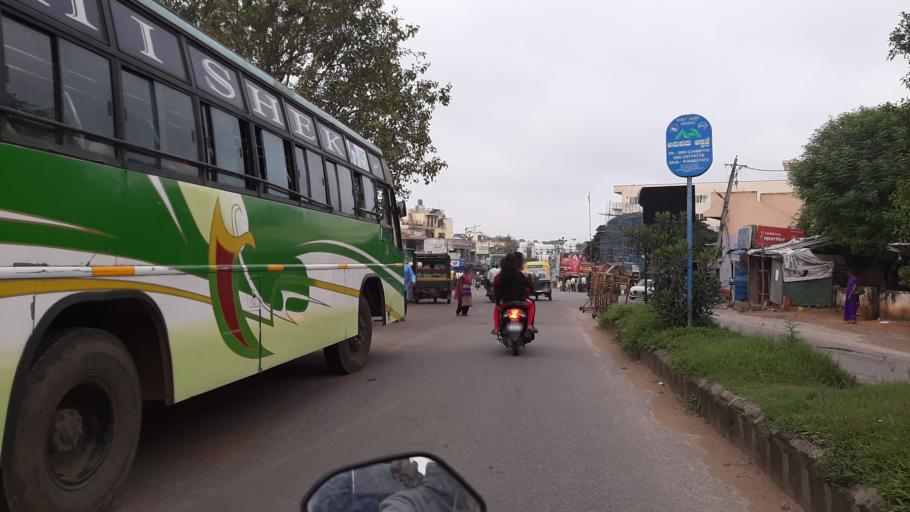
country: IN
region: Karnataka
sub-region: Bangalore Rural
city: Nelamangala
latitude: 12.9661
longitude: 77.4007
